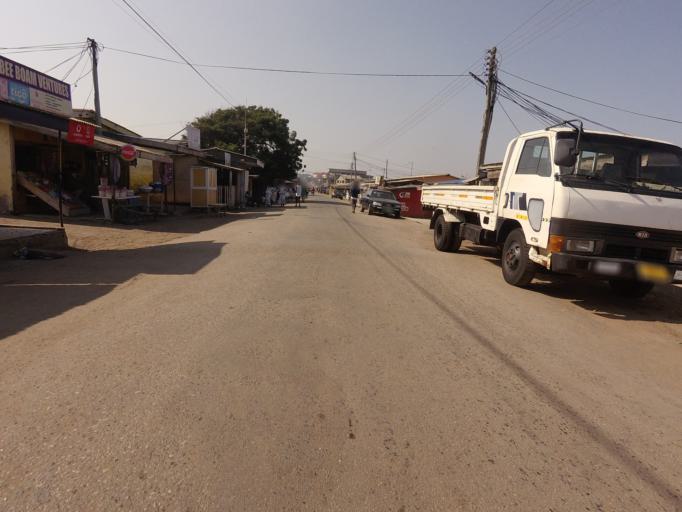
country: GH
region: Greater Accra
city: Teshi Old Town
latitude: 5.5805
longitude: -0.1010
